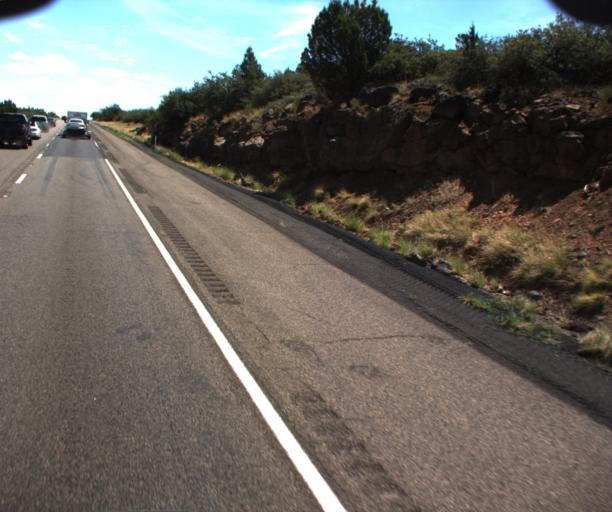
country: US
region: Arizona
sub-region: Yavapai County
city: Village of Oak Creek (Big Park)
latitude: 34.7741
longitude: -111.6337
